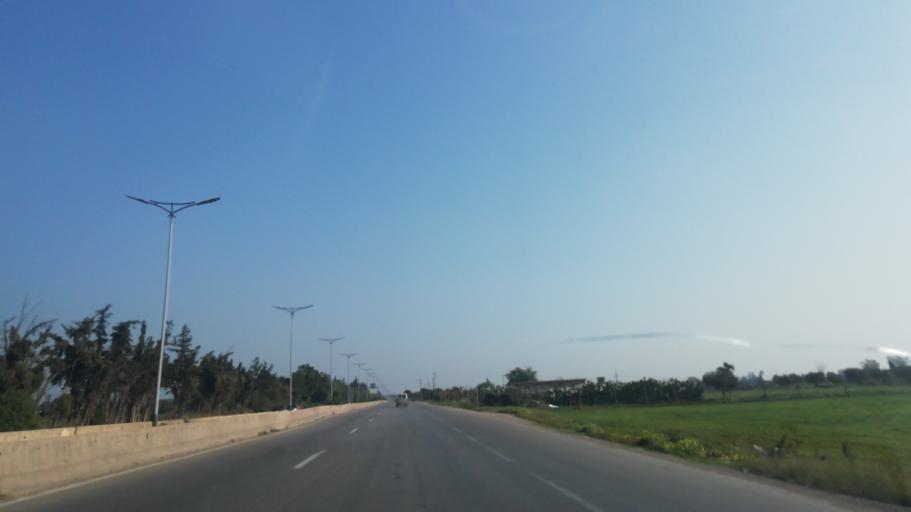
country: DZ
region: Oran
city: Bou Tlelis
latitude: 35.5728
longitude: -0.8771
